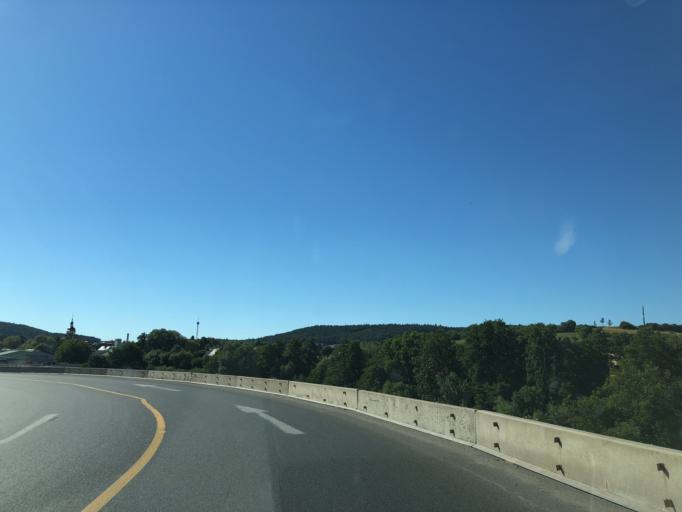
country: DE
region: Bavaria
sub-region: Regierungsbezirk Unterfranken
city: Geiselwind
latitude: 49.7704
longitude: 10.4802
